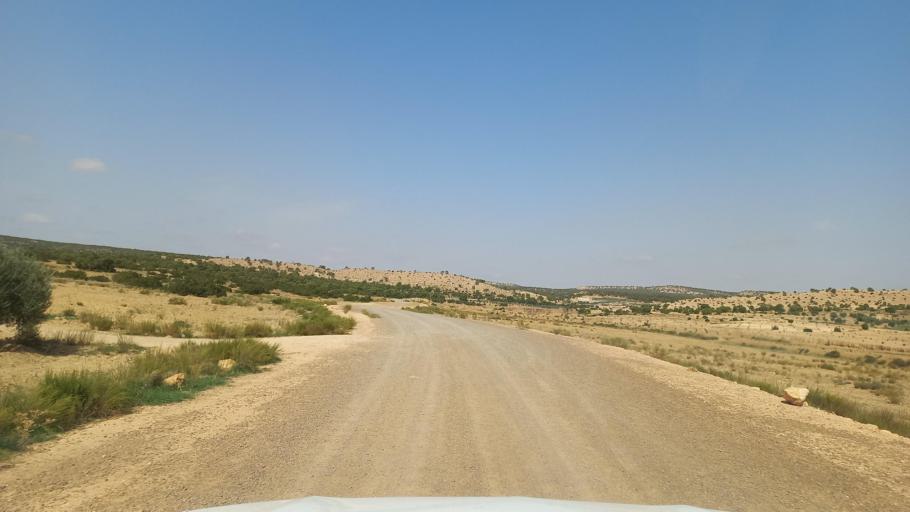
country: TN
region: Al Qasrayn
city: Sbiba
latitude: 35.3893
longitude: 8.9550
